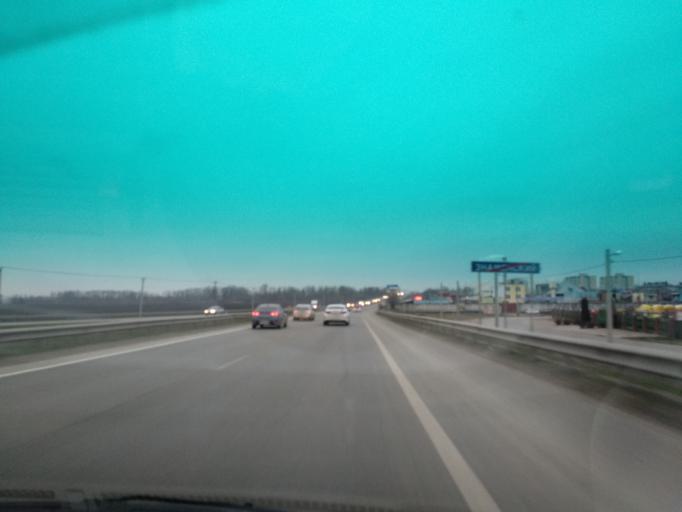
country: RU
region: Krasnodarskiy
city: Pashkovskiy
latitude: 45.0523
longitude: 39.1301
